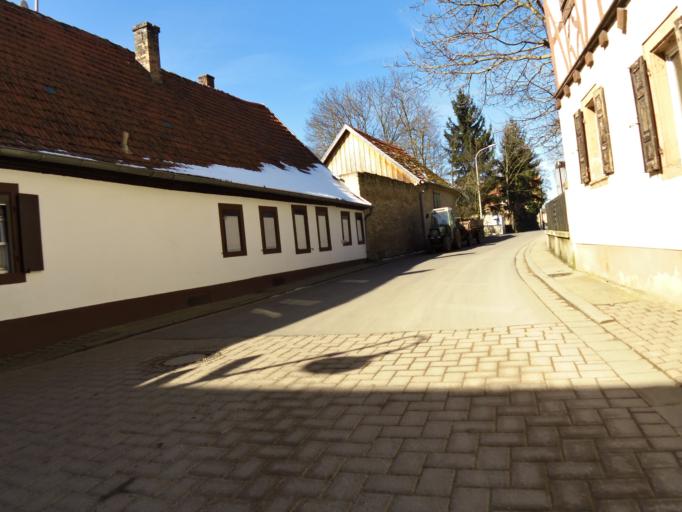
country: DE
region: Rheinland-Pfalz
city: Einselthum
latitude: 49.6433
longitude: 8.1345
